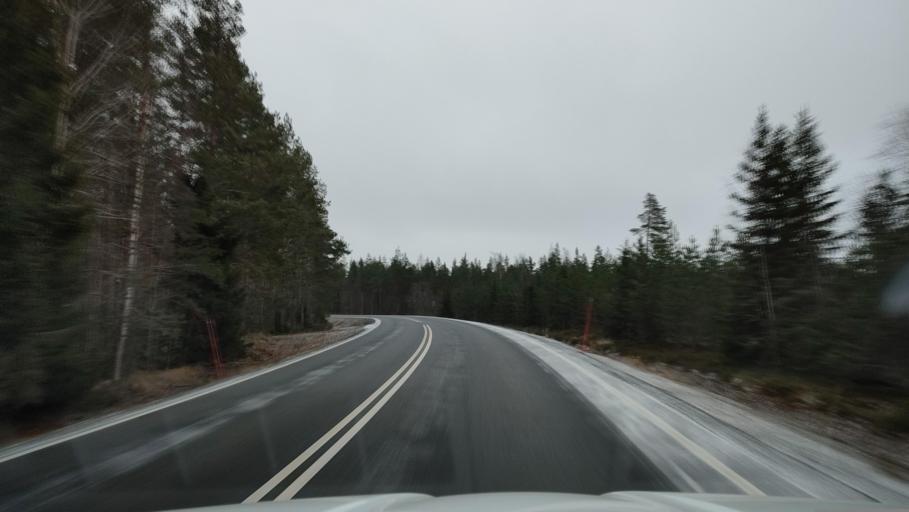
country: FI
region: Southern Ostrobothnia
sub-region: Suupohja
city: Karijoki
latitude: 62.2903
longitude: 21.6516
